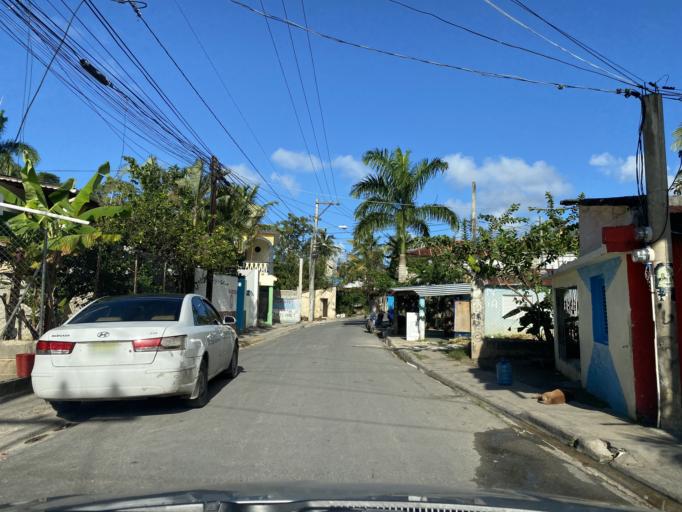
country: DO
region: Samana
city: Las Terrenas
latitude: 19.3132
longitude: -69.5452
